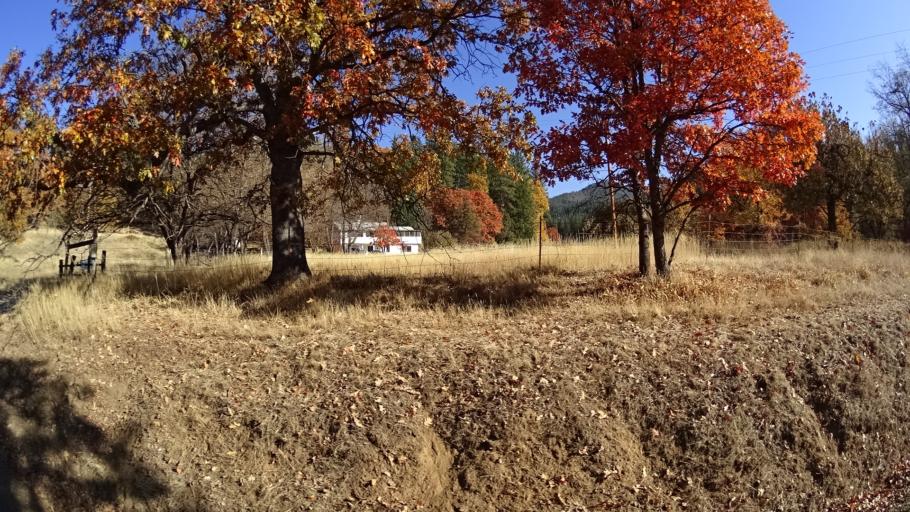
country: US
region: California
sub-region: Siskiyou County
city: Yreka
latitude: 41.6384
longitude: -122.9838
